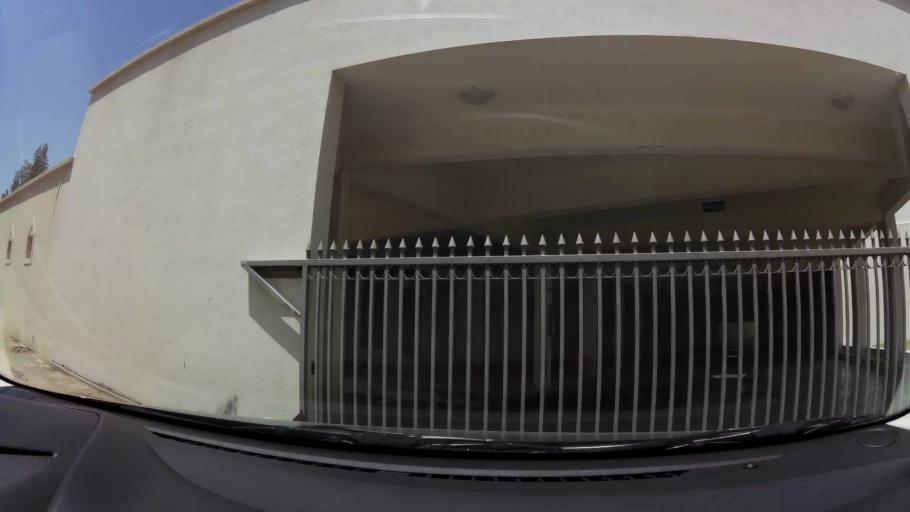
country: OM
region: Muhafazat Masqat
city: Bawshar
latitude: 23.6005
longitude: 58.4755
